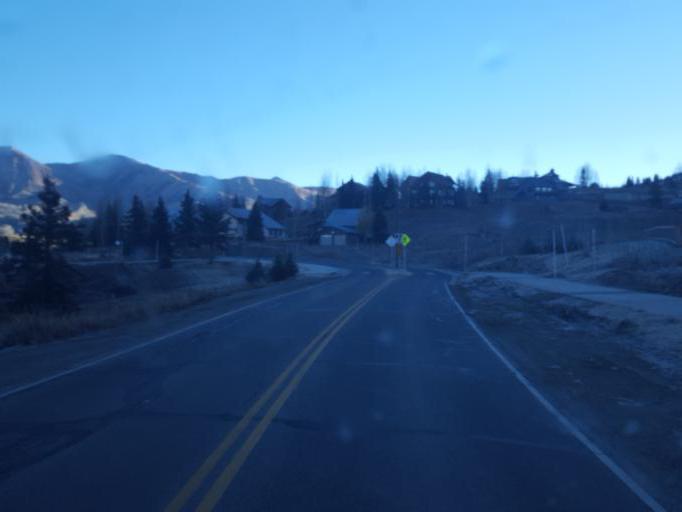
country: US
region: Colorado
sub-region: Gunnison County
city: Crested Butte
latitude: 38.9092
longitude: -106.9686
